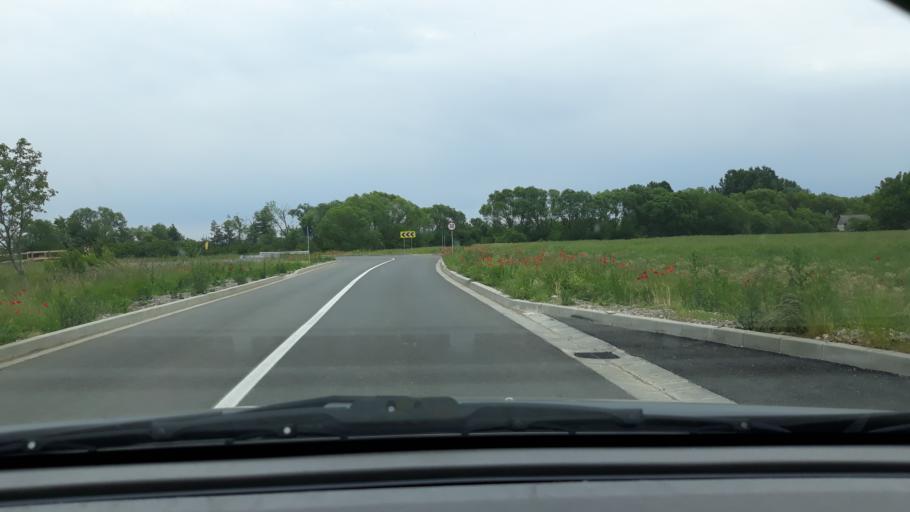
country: RO
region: Bihor
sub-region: Comuna Osorheiu
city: Osorheiu
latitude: 47.0658
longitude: 22.0386
